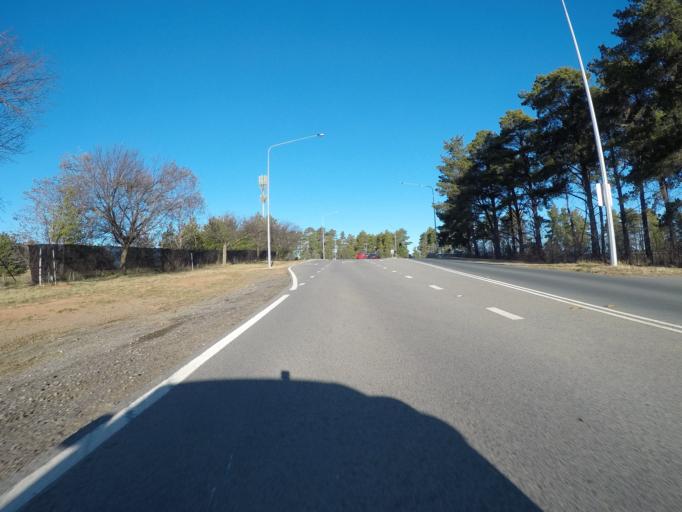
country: AU
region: Australian Capital Territory
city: Forrest
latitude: -35.3122
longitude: 149.0819
